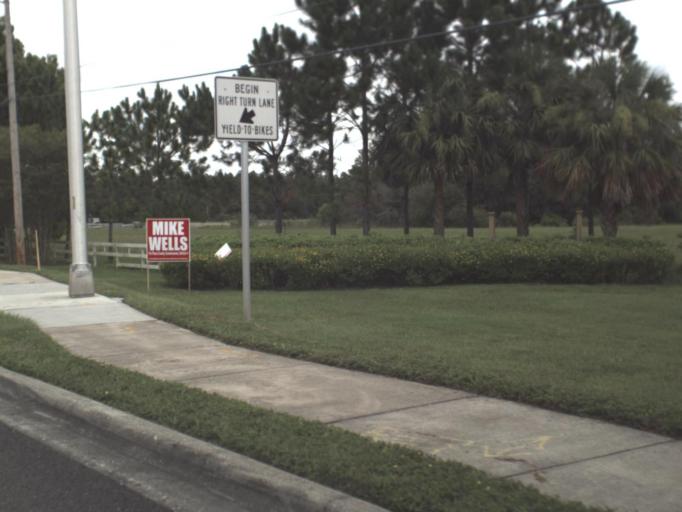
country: US
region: Florida
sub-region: Pasco County
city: Trinity
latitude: 28.1985
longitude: -82.6452
